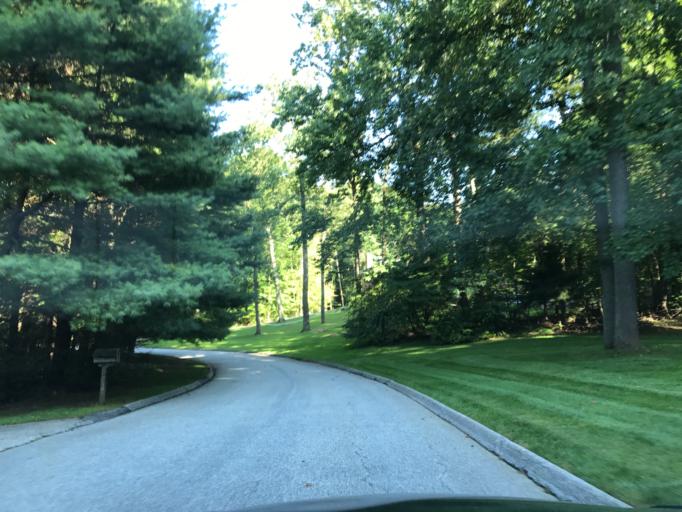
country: US
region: Maryland
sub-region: Baltimore County
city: Hunt Valley
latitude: 39.5313
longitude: -76.6072
